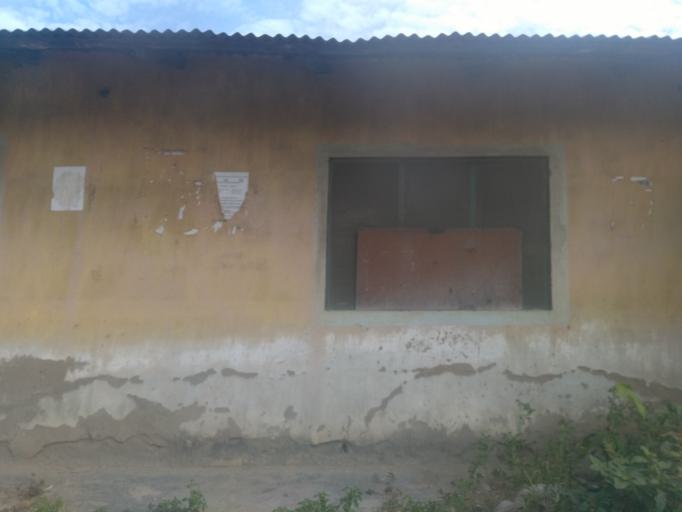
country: TZ
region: Zanzibar Urban/West
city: Zanzibar
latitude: -6.1592
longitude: 39.2040
